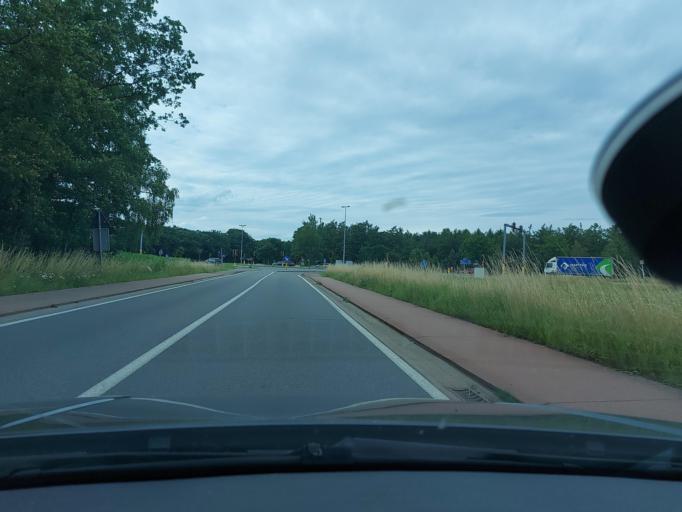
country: BE
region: Flanders
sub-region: Provincie Antwerpen
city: Balen
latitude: 51.2086
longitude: 5.2192
